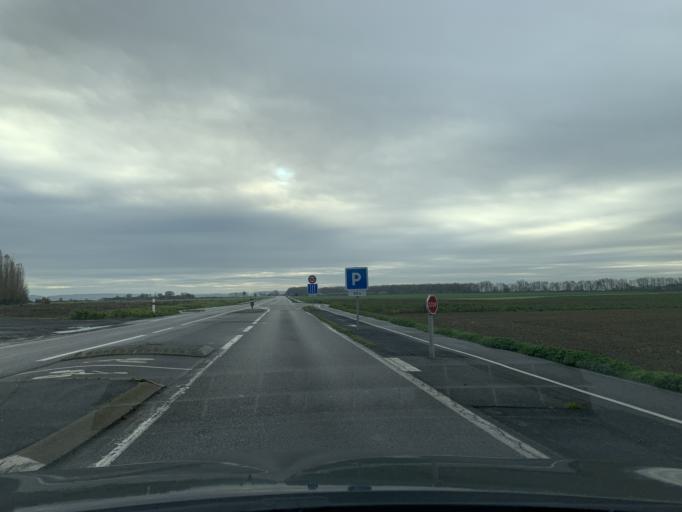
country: FR
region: Nord-Pas-de-Calais
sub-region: Departement du Nord
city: Goeulzin
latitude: 50.3362
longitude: 3.1005
